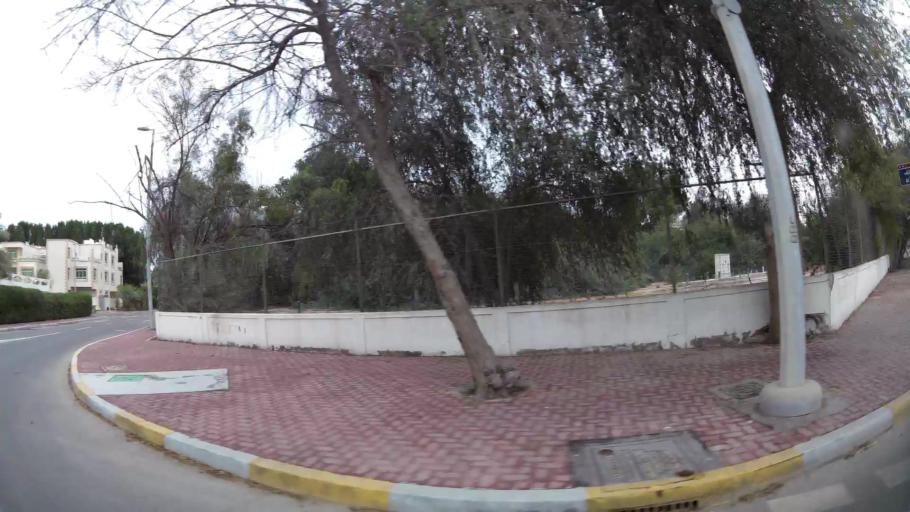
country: AE
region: Abu Dhabi
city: Abu Dhabi
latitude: 24.4285
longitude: 54.3771
